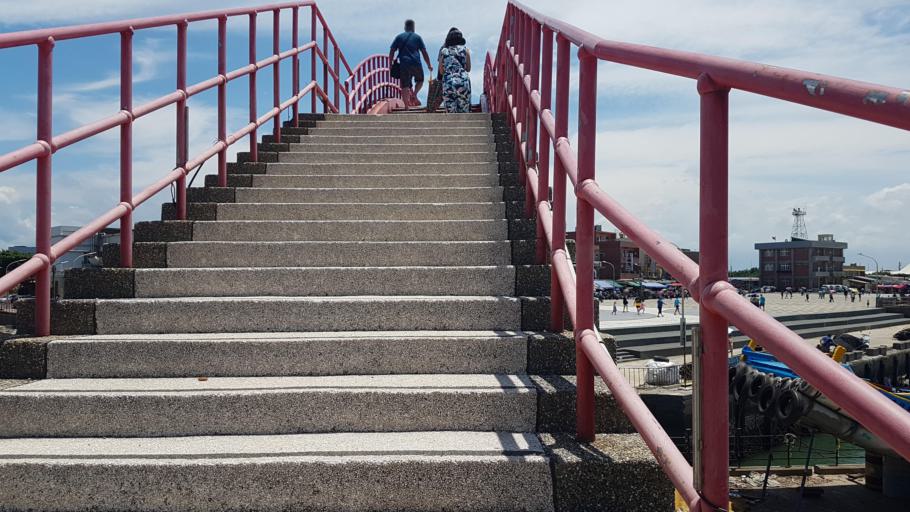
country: TW
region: Taiwan
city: Taoyuan City
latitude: 25.1180
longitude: 121.2447
